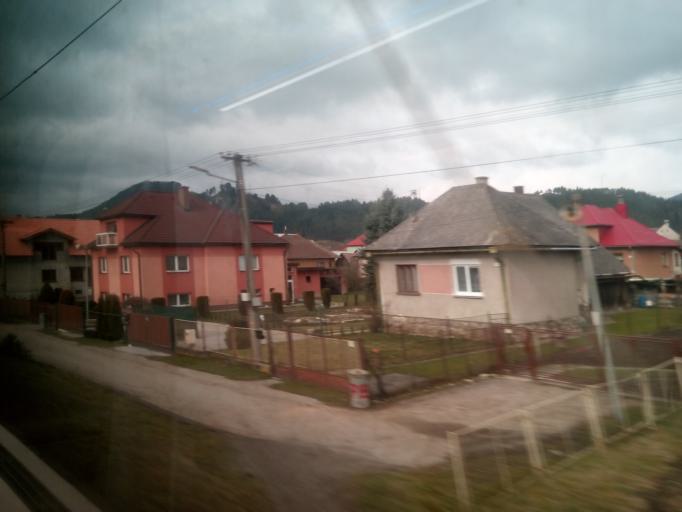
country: SK
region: Zilinsky
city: Ruzomberok
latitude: 49.0874
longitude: 19.3530
